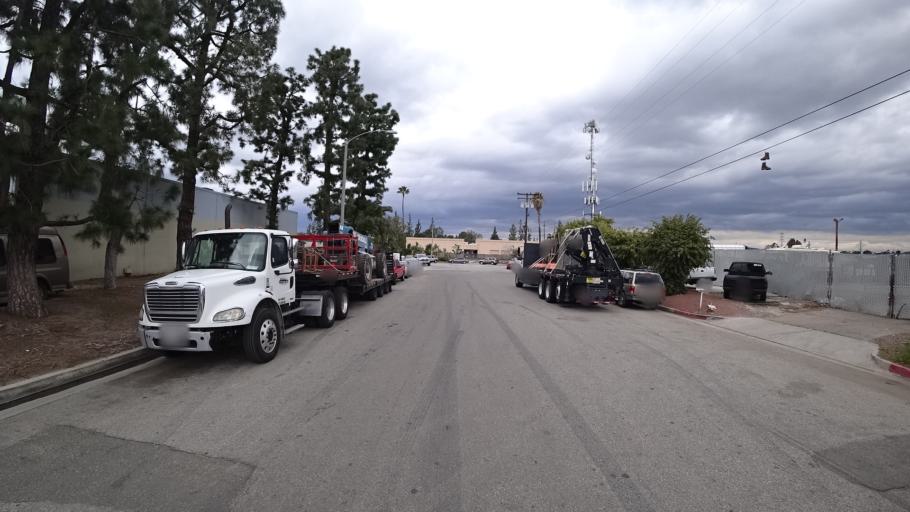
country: US
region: California
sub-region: Orange County
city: Placentia
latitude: 33.8617
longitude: -117.8680
